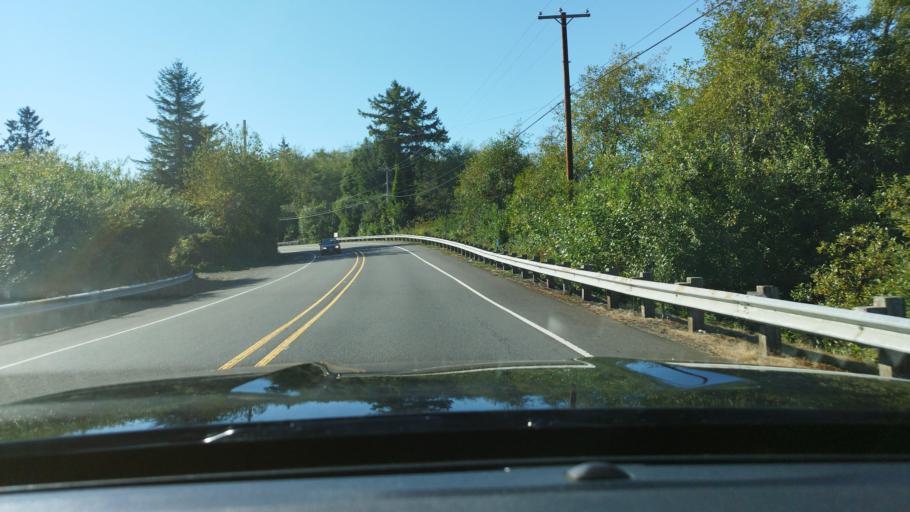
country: US
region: Oregon
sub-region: Clatsop County
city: Warrenton
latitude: 46.1538
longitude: -123.9135
